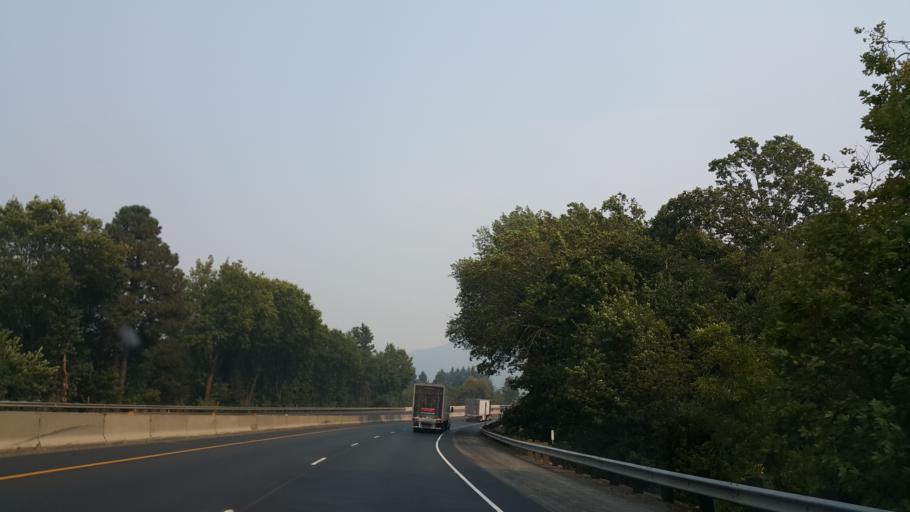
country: US
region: Oregon
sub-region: Jackson County
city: Rogue River
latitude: 42.4341
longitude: -123.1769
